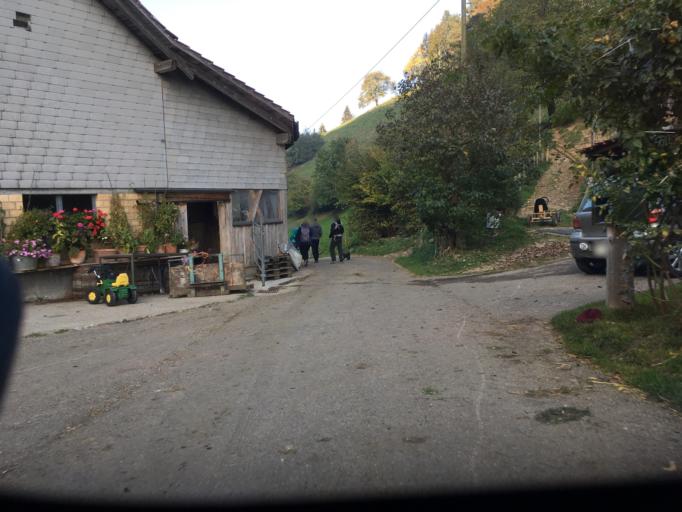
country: CH
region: Saint Gallen
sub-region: Wahlkreis Toggenburg
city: Lichtensteig
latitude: 47.3241
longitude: 9.0518
